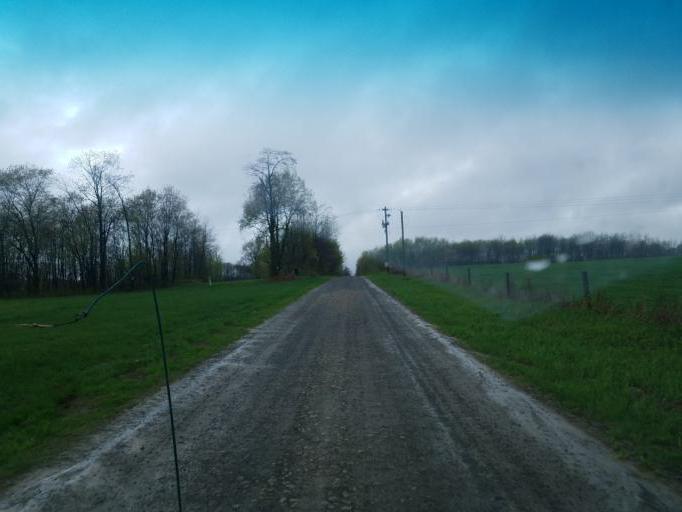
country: US
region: Pennsylvania
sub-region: Tioga County
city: Westfield
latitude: 41.9809
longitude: -77.7070
